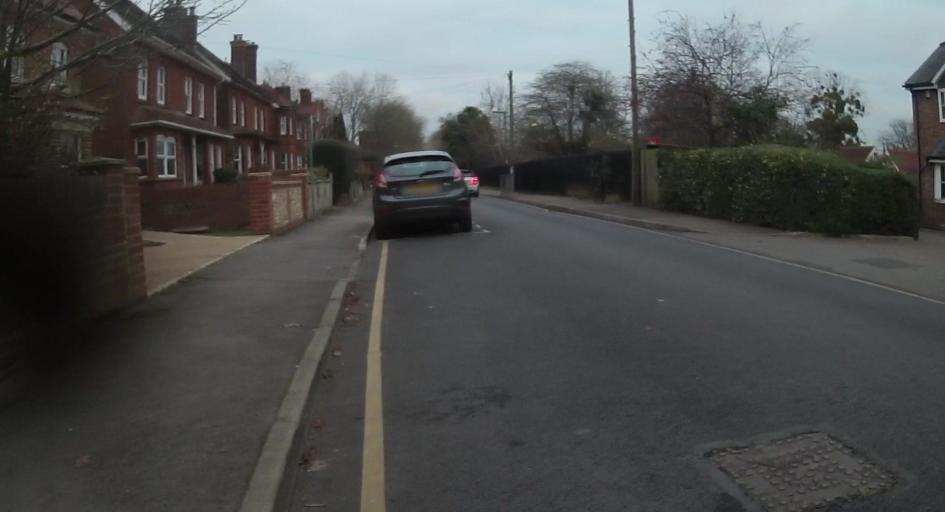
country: GB
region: England
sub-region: Surrey
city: Farnham
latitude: 51.2137
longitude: -0.8081
